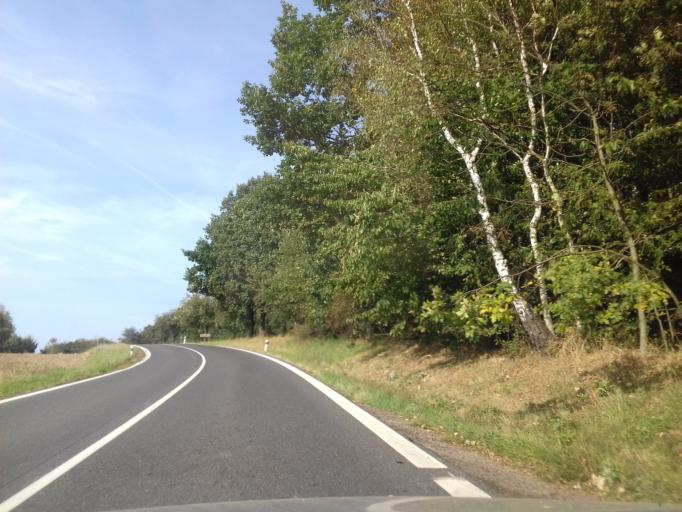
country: CZ
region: Central Bohemia
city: Kosova Hora
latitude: 49.6604
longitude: 14.5462
